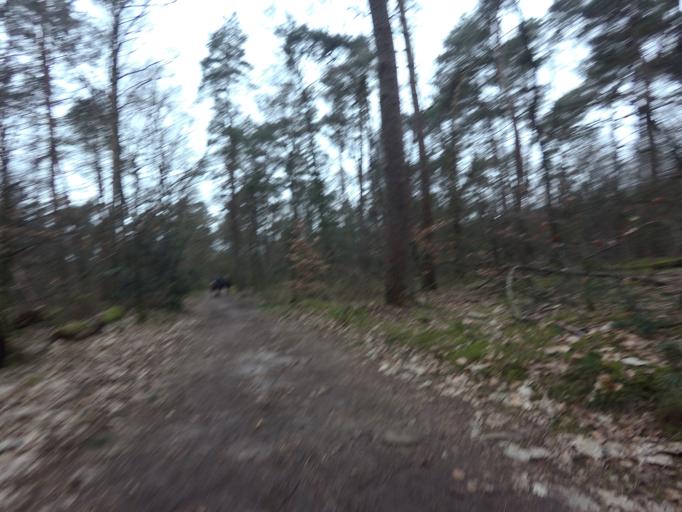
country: NL
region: Utrecht
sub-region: Gemeente Utrechtse Heuvelrug
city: Doorn
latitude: 52.0428
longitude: 5.3593
